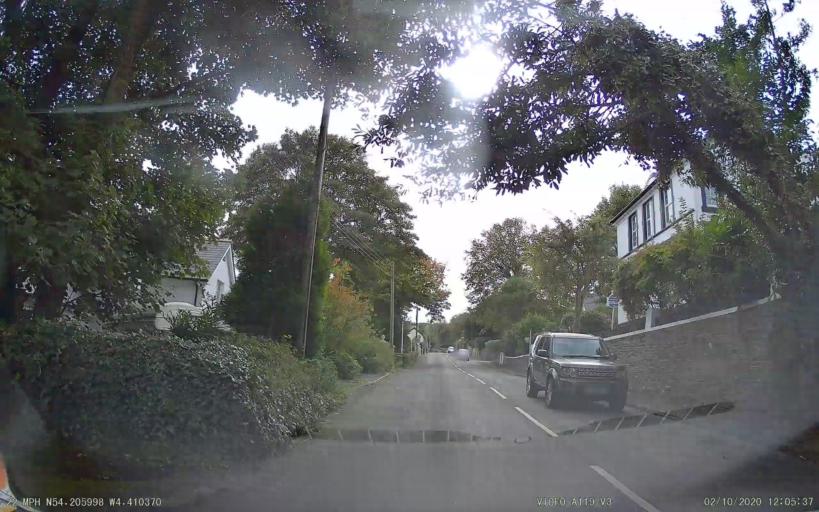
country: IM
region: Laxey
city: Laxey
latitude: 54.2060
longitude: -4.4104
